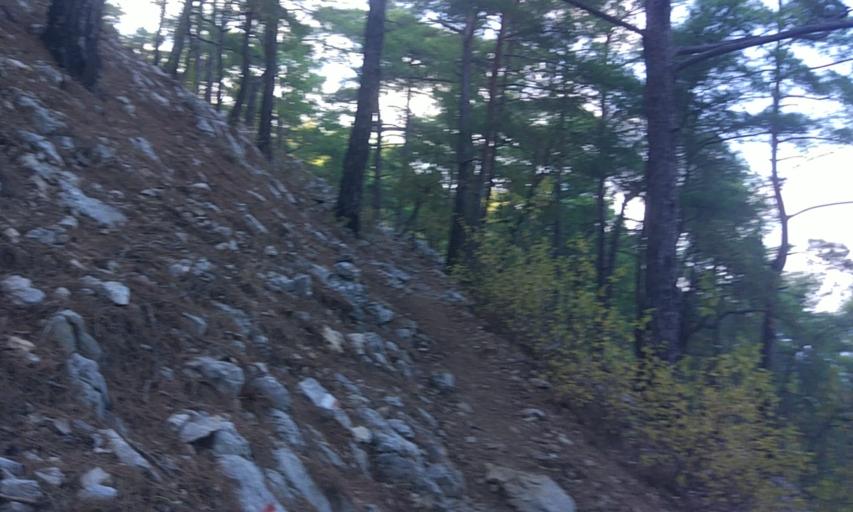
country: TR
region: Antalya
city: Tekirova
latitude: 36.3634
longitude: 30.4783
